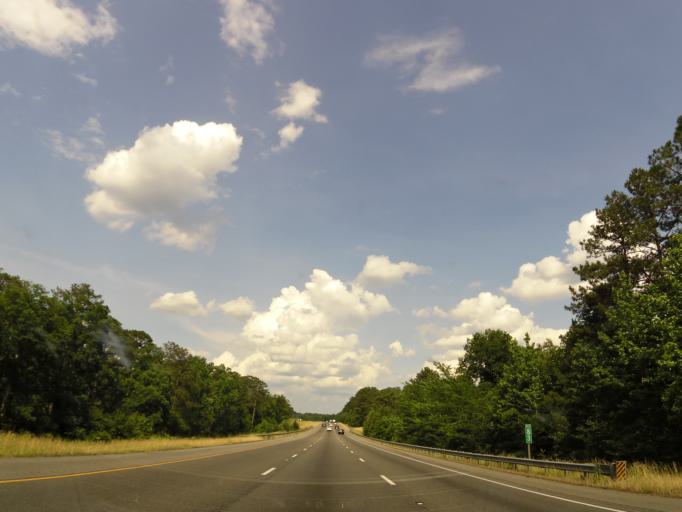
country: US
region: Alabama
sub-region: Tuscaloosa County
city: Coaling
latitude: 33.1832
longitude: -87.3558
